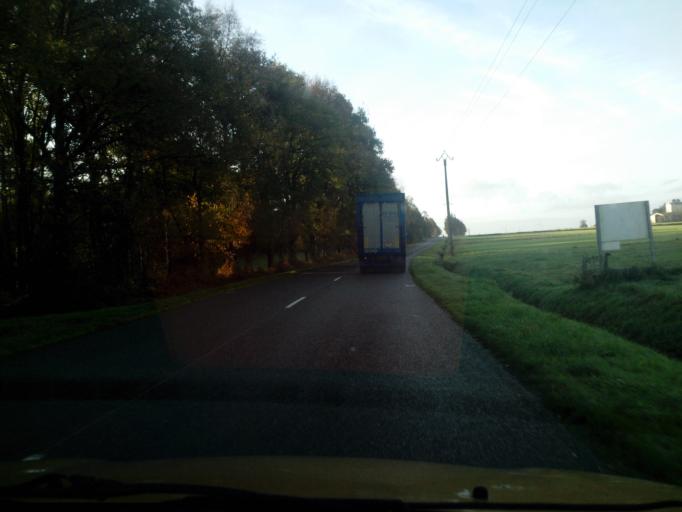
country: FR
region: Brittany
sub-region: Departement du Morbihan
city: Guilliers
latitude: 48.0344
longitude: -2.4218
